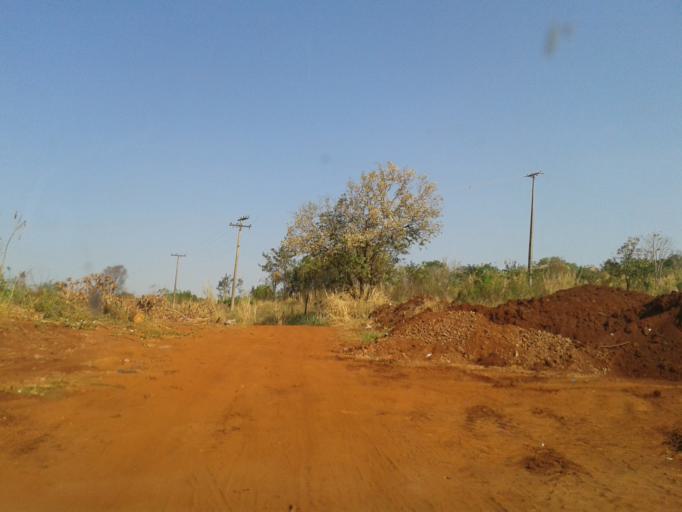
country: BR
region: Minas Gerais
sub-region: Ituiutaba
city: Ituiutaba
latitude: -18.9645
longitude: -49.4771
